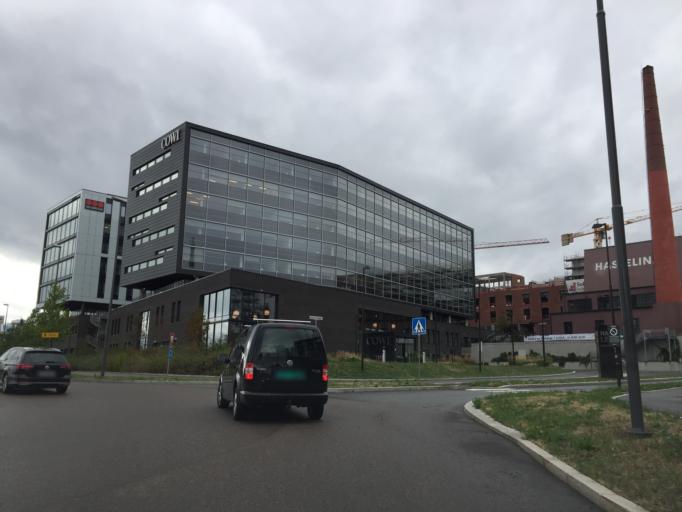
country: NO
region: Oslo
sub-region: Oslo
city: Oslo
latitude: 59.9271
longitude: 10.7984
